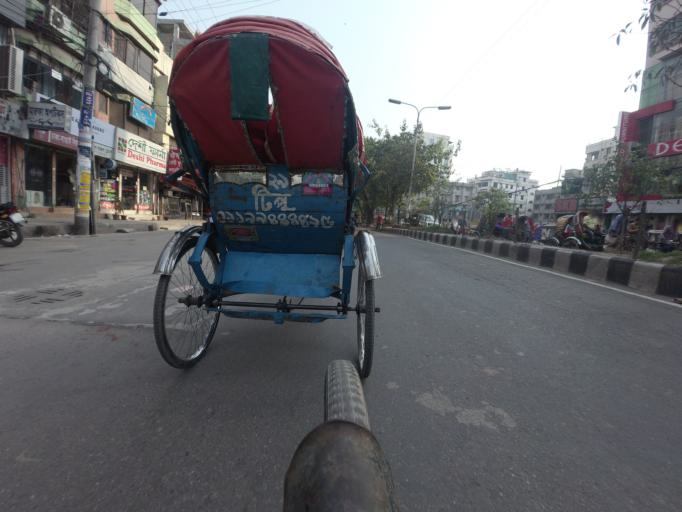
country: BD
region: Dhaka
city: Azimpur
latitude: 23.7692
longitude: 90.3586
